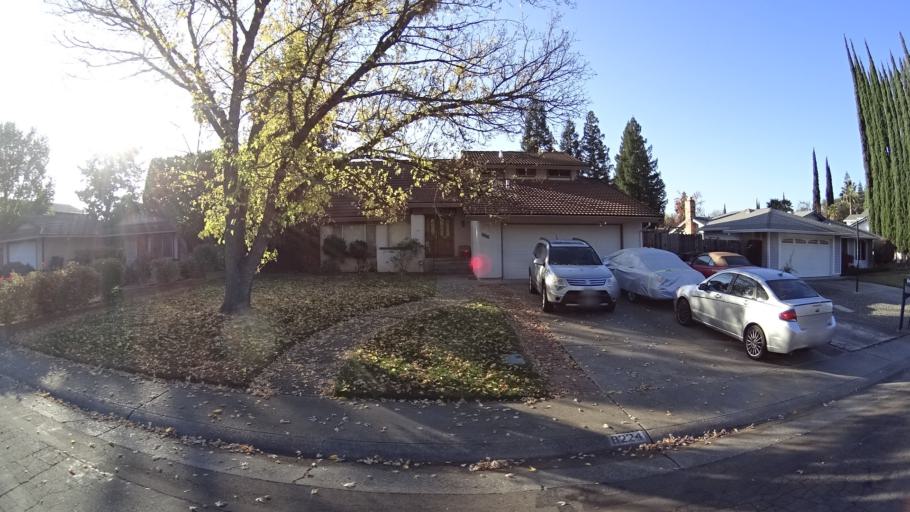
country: US
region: California
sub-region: Sacramento County
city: Citrus Heights
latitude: 38.7173
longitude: -121.2559
